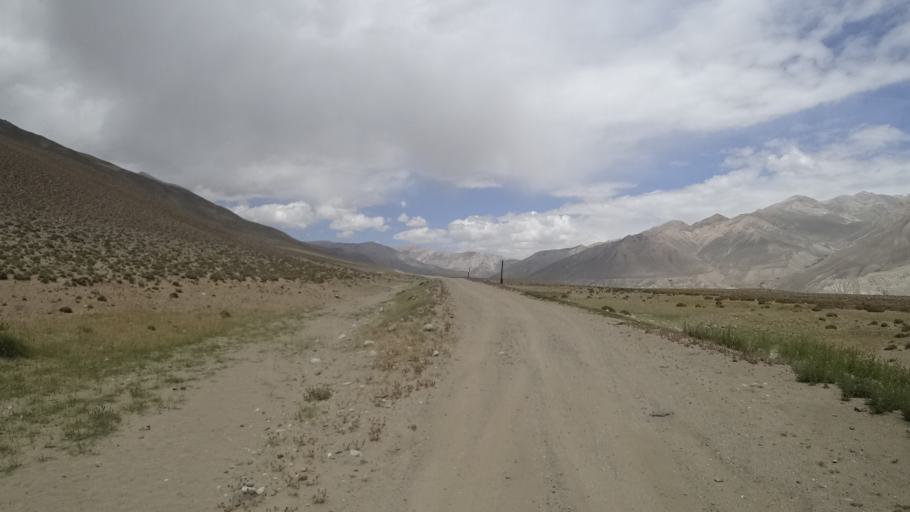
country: AF
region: Badakhshan
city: Khandud
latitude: 37.1321
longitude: 72.7324
